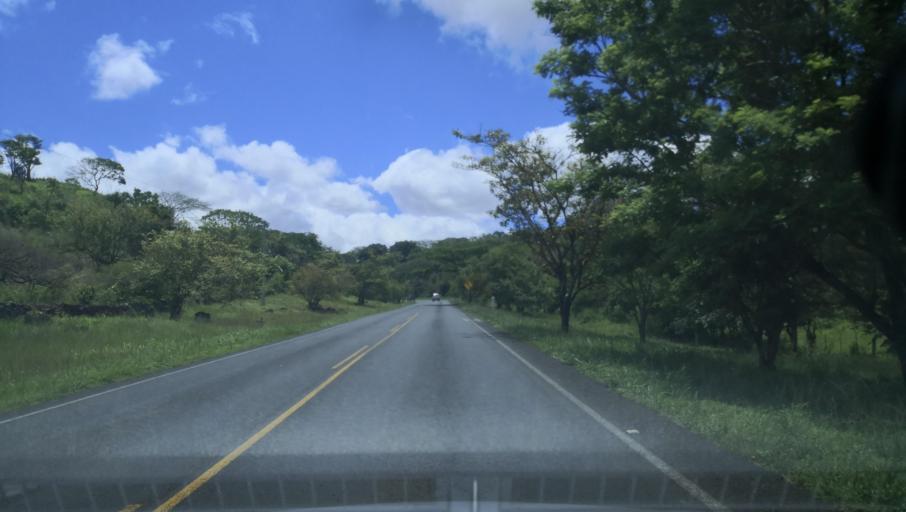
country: NI
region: Esteli
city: Esteli
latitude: 13.2089
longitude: -86.3770
